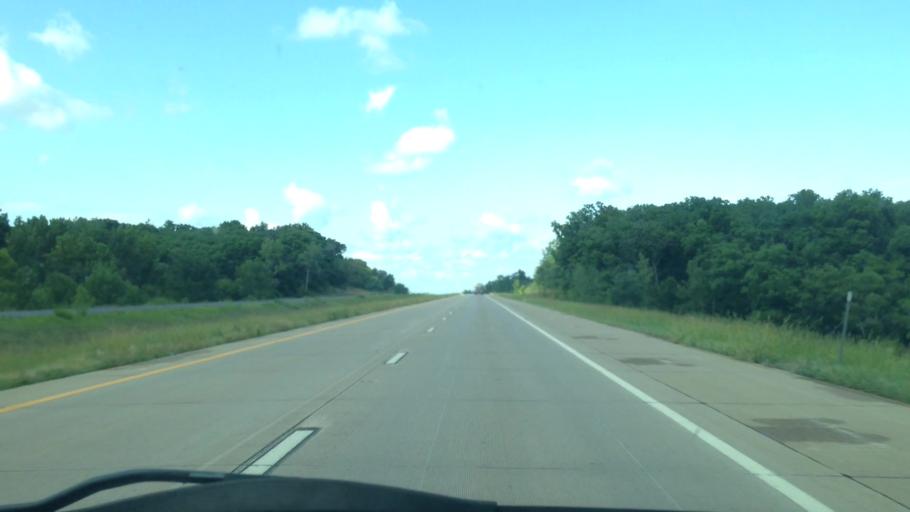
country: US
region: Missouri
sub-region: Lewis County
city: Canton
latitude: 40.1598
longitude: -91.5330
